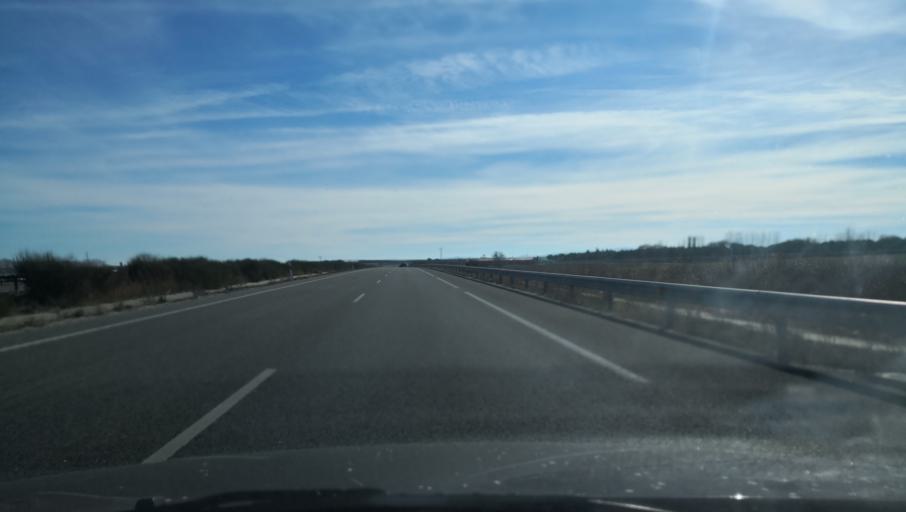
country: ES
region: Castille and Leon
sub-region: Provincia de Salamanca
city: Cantaracillo
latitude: 40.9041
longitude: -5.1770
